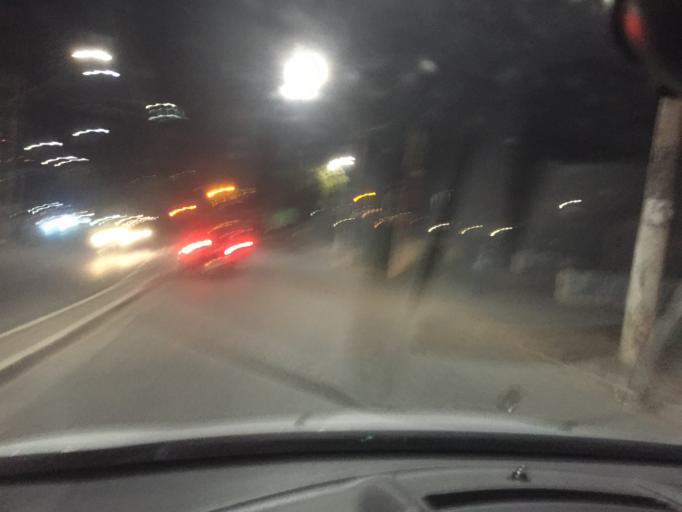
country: BR
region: Sao Paulo
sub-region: Varzea Paulista
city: Varzea Paulista
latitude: -23.2099
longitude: -46.8300
